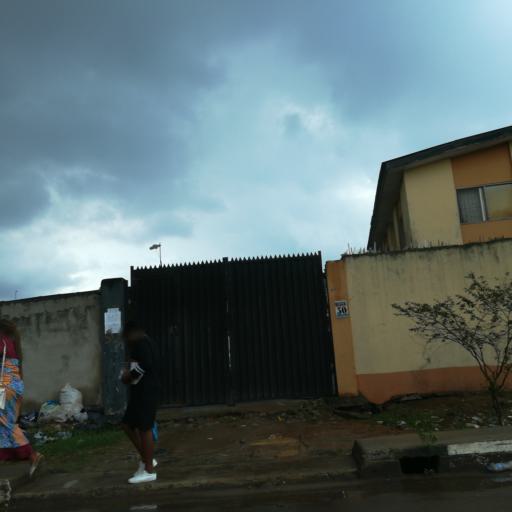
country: NG
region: Lagos
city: Agege
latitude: 6.5906
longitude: 3.2947
